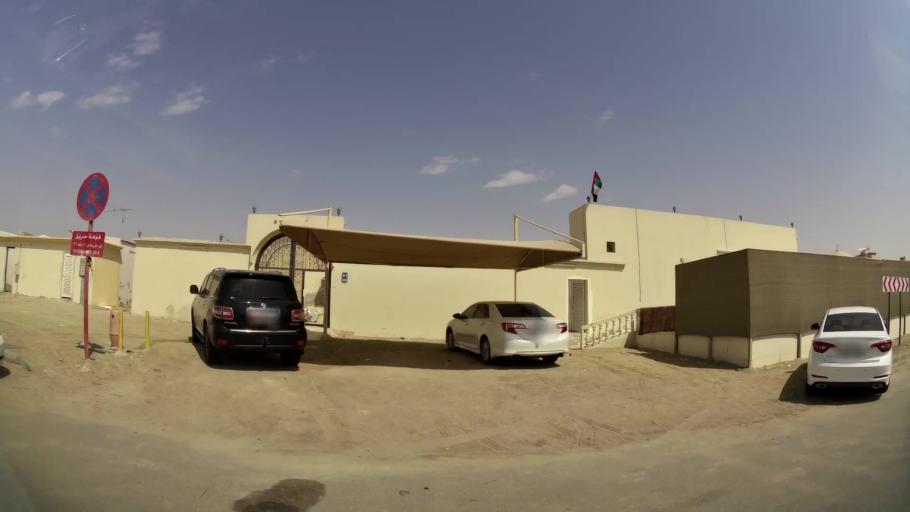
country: AE
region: Abu Dhabi
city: Abu Dhabi
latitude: 24.2922
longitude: 54.6522
